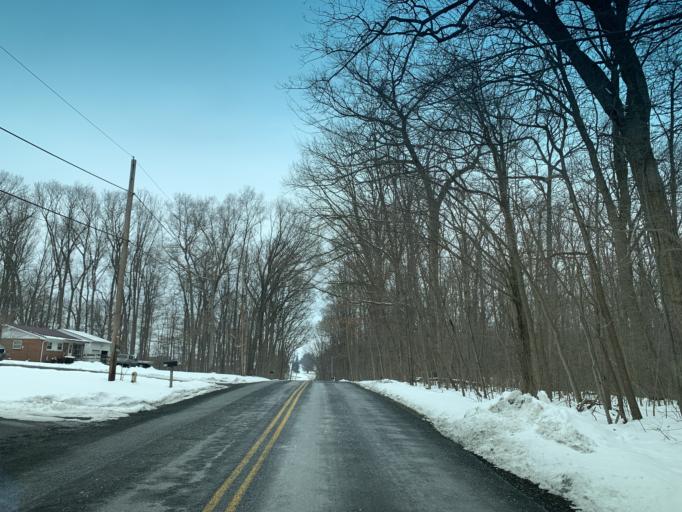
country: US
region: Pennsylvania
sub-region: York County
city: Susquehanna Trails
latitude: 39.7053
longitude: -76.4215
